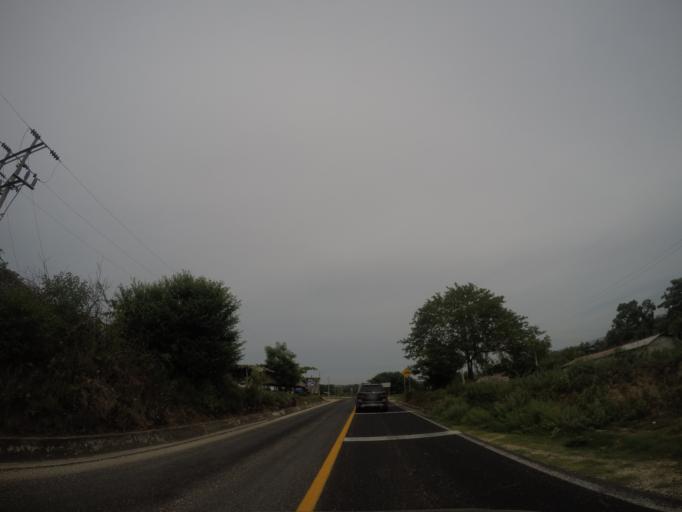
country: MX
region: Oaxaca
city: San Pedro Mixtepec
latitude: 15.9504
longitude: -97.2818
